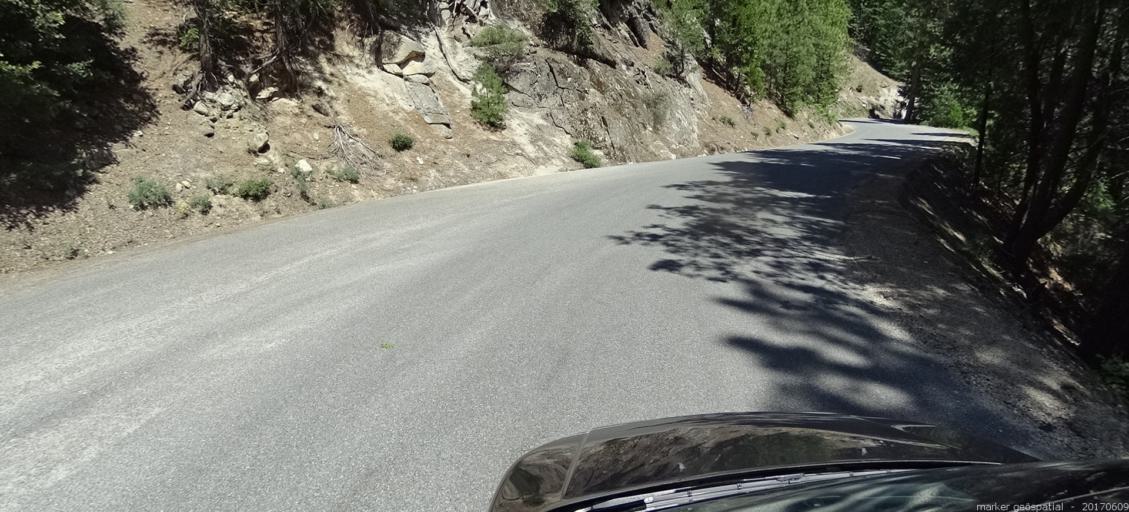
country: US
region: California
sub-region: Siskiyou County
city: Yreka
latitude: 41.4293
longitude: -122.9344
